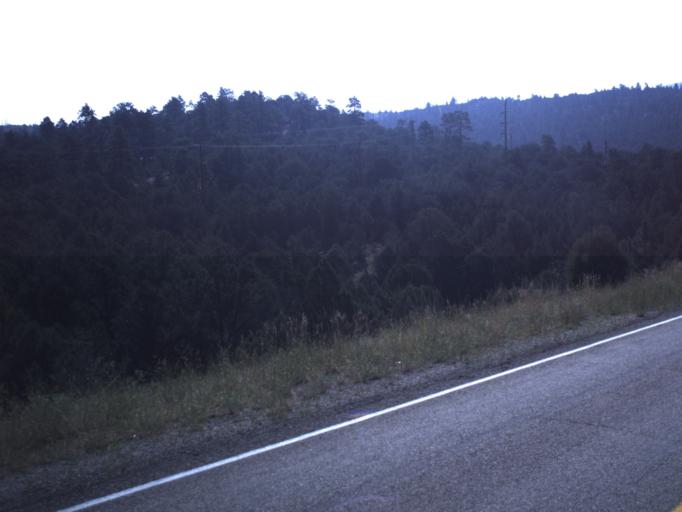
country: US
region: Utah
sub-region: Daggett County
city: Manila
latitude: 40.9151
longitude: -109.4140
